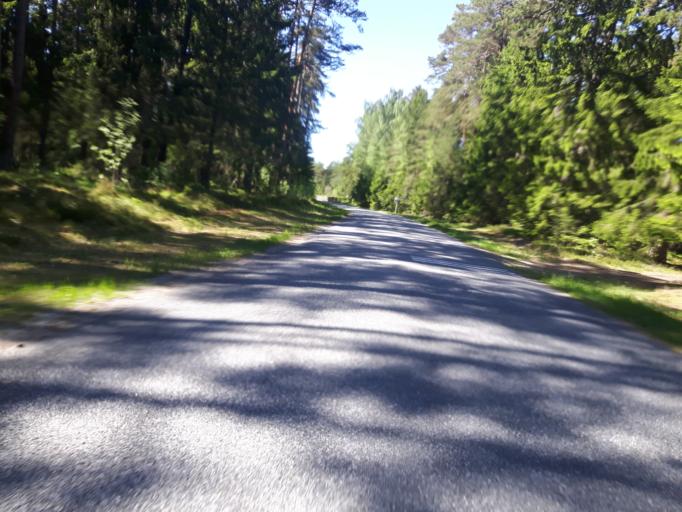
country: EE
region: Laeaene-Virumaa
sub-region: Haljala vald
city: Haljala
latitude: 59.5750
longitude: 26.2784
